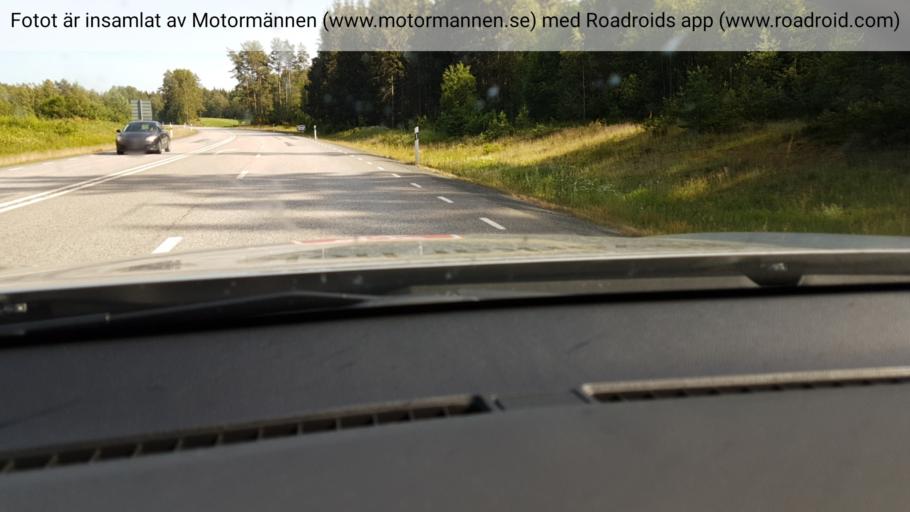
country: SE
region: Joenkoeping
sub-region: Aneby Kommun
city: Aneby
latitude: 57.7738
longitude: 14.8878
